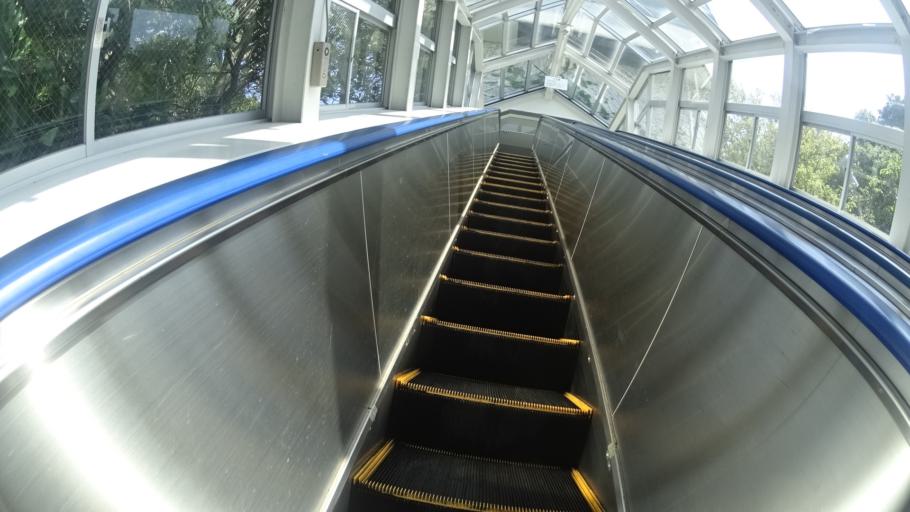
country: JP
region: Tokushima
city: Narutocho-mitsuishi
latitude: 34.2367
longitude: 134.6400
